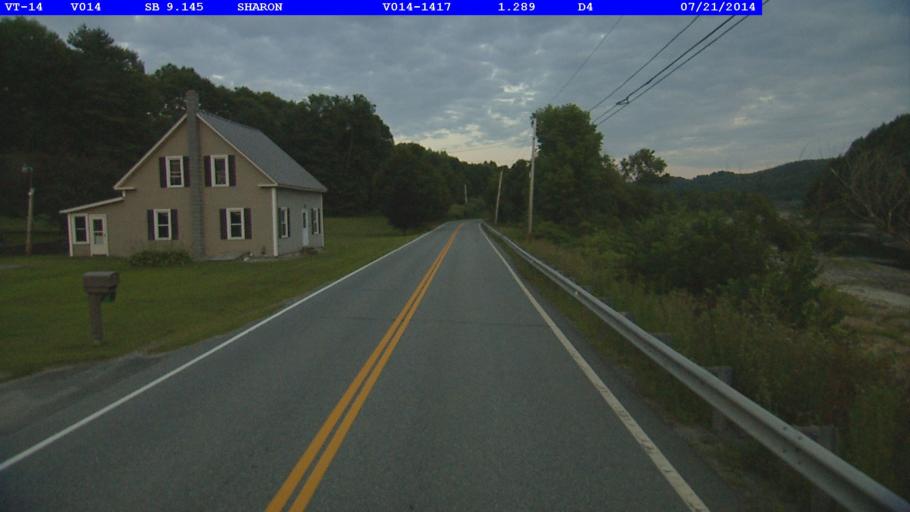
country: US
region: Vermont
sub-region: Windsor County
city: Woodstock
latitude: 43.7378
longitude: -72.4366
